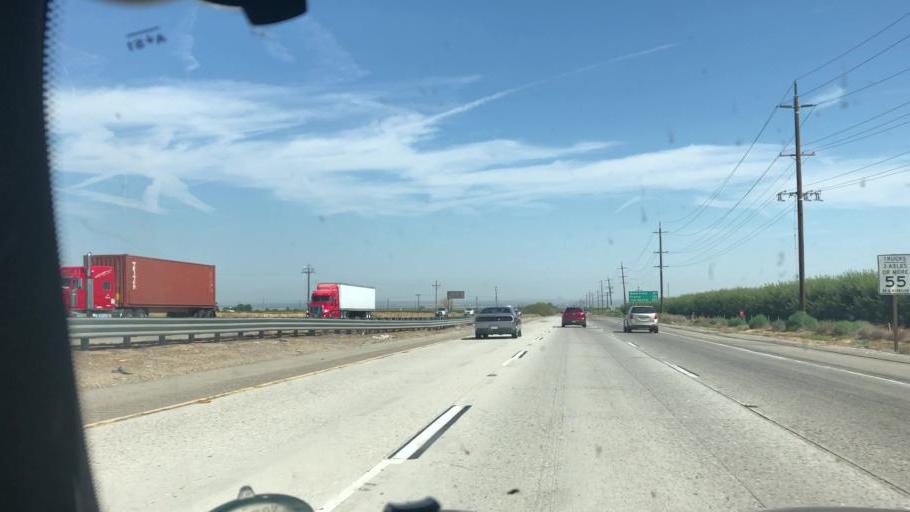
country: US
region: California
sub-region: Kern County
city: Frazier Park
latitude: 35.0227
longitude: -118.9567
